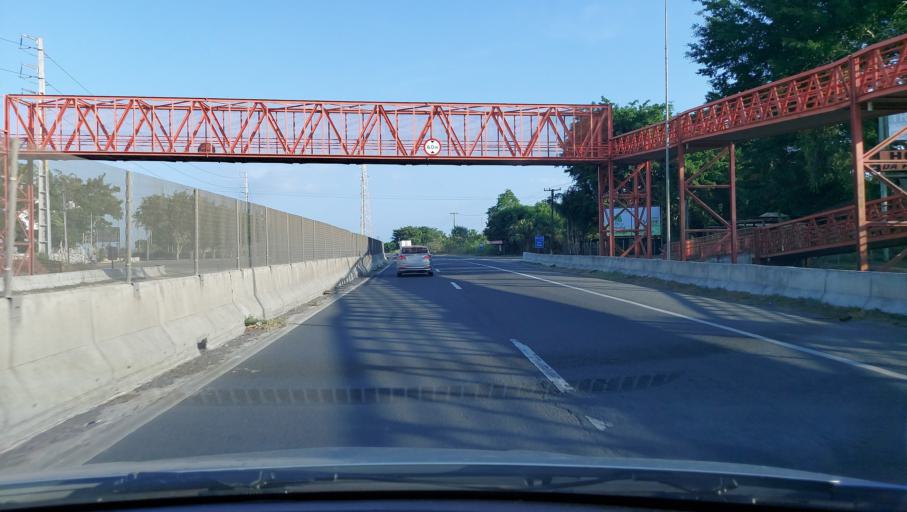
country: BR
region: Bahia
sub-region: Conceicao Do Jacuipe
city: Conceicao do Jacuipe
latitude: -12.3882
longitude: -38.7887
